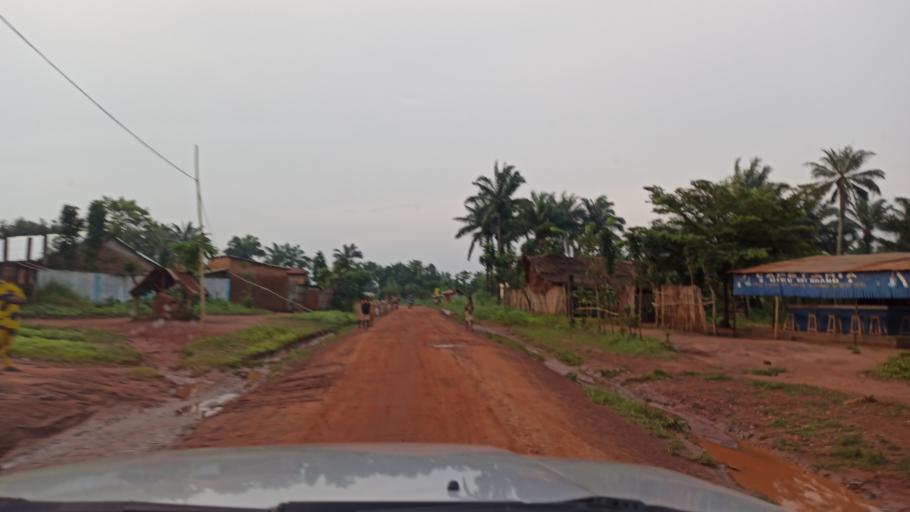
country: BJ
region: Queme
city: Porto-Novo
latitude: 6.5436
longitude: 2.6194
